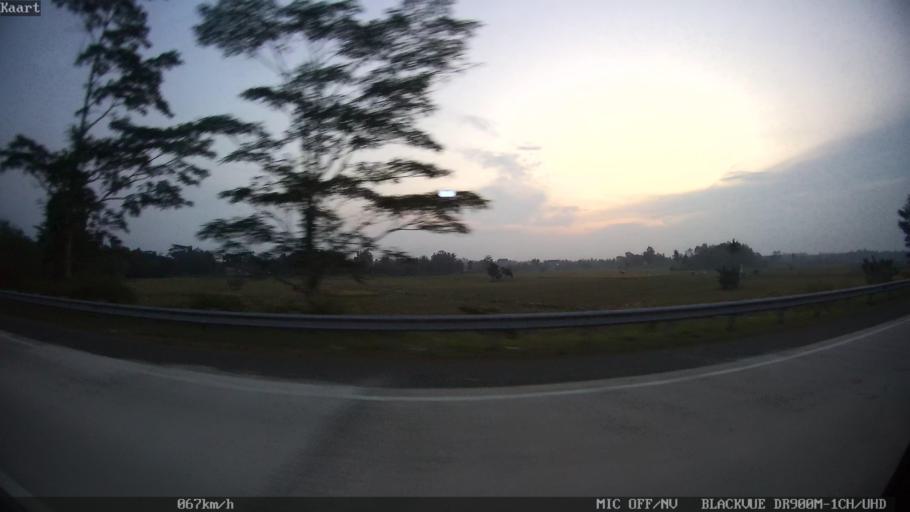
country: ID
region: Lampung
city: Sidorejo
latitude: -5.5937
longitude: 105.5490
